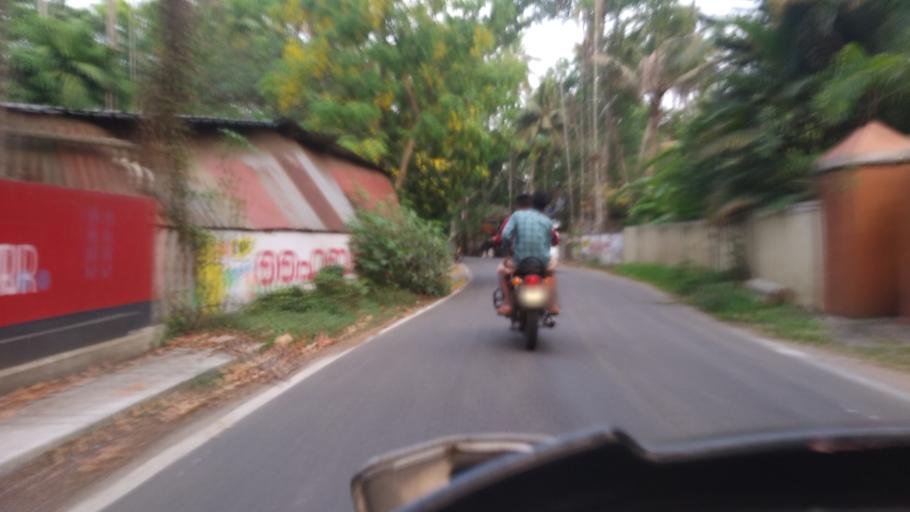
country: IN
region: Kerala
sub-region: Thrissur District
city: Kodungallur
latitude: 10.1658
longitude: 76.2028
